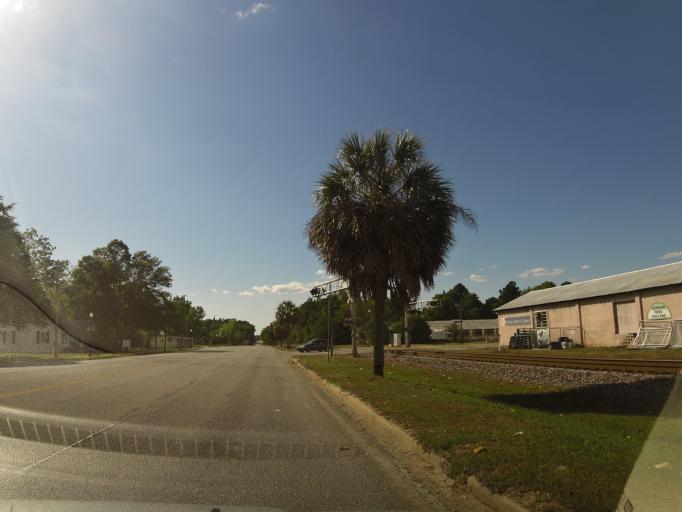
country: US
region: South Carolina
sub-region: Allendale County
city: Fairfax
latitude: 32.9607
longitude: -81.2397
